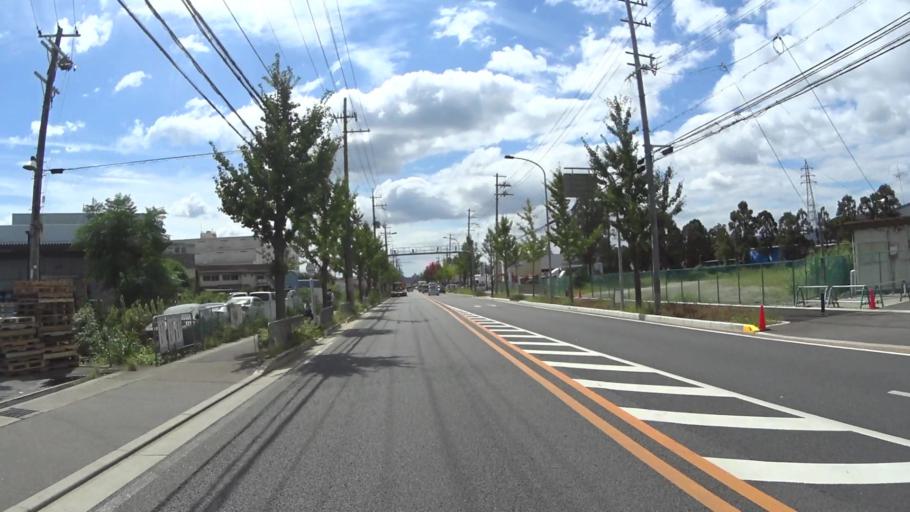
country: JP
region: Kyoto
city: Muko
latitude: 34.9199
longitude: 135.7315
